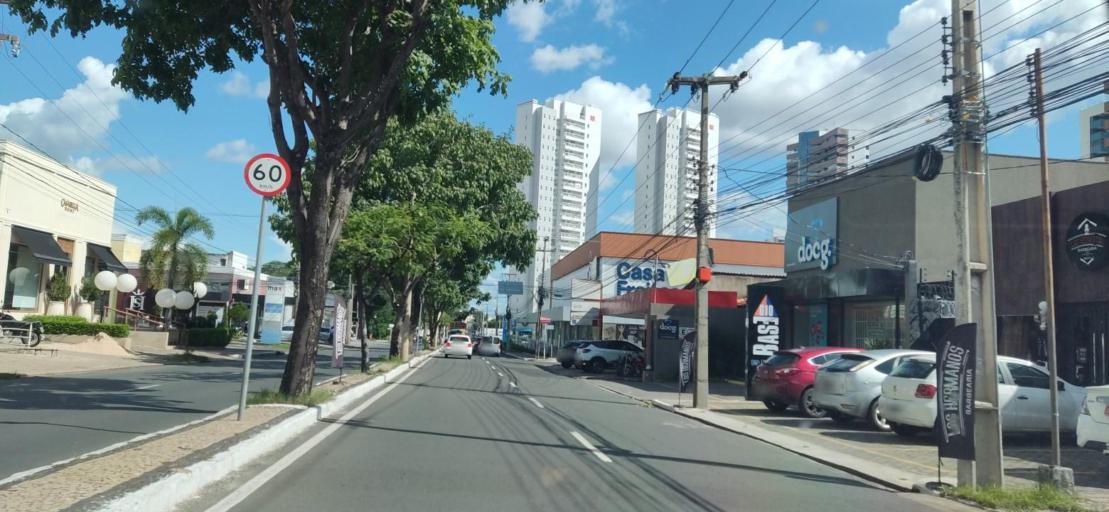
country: BR
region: Piaui
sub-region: Teresina
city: Teresina
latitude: -5.0749
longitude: -42.7912
